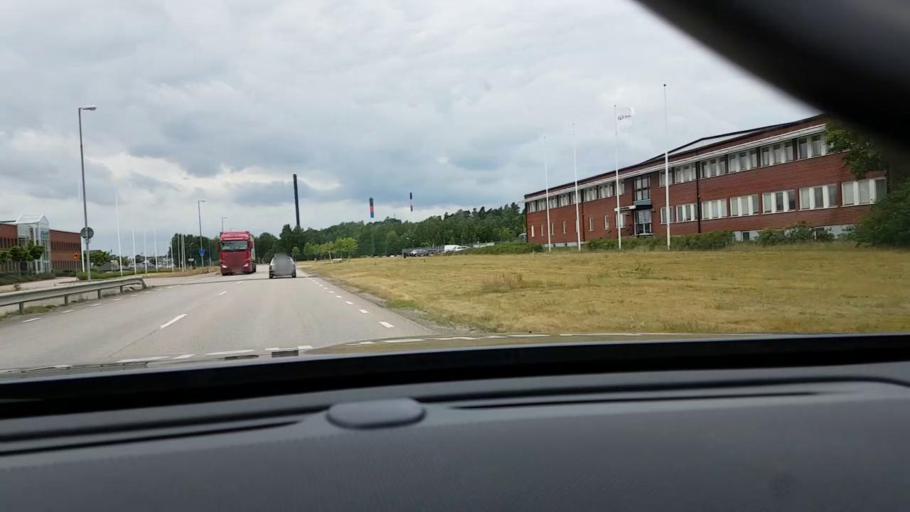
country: SE
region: Skane
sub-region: Hassleholms Kommun
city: Hassleholm
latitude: 56.1585
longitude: 13.8065
